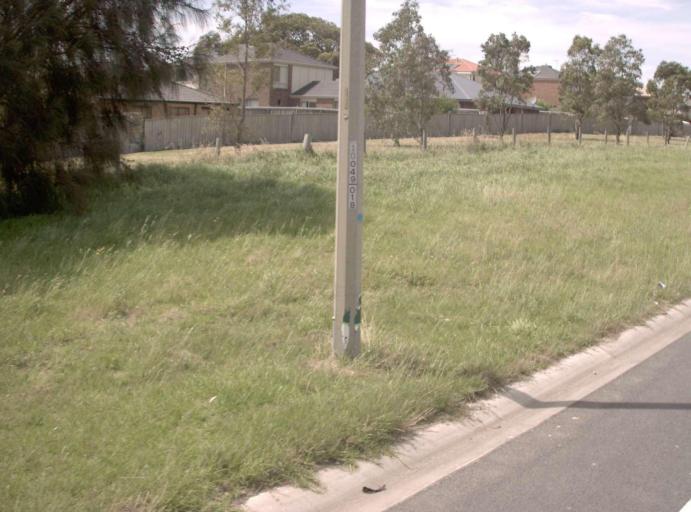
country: AU
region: Victoria
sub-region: Casey
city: Lynbrook
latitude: -38.0579
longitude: 145.2435
